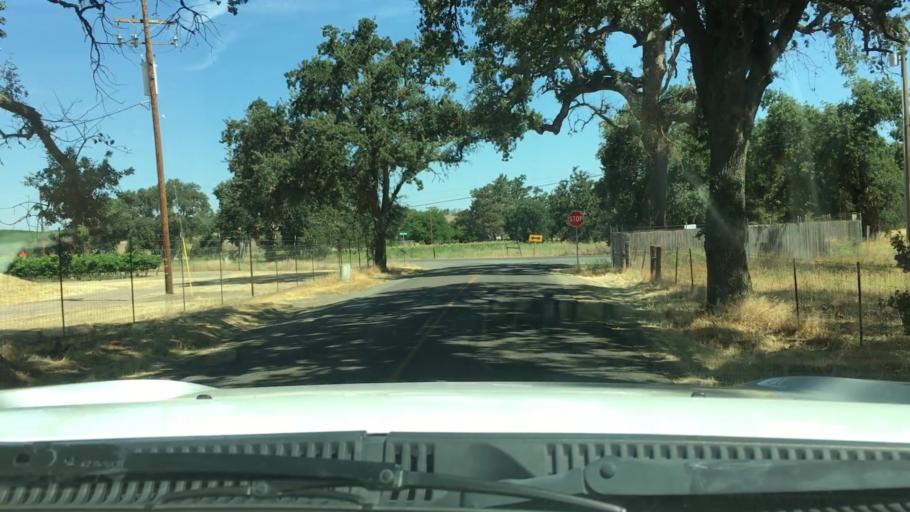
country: US
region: California
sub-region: San Luis Obispo County
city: Paso Robles
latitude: 35.5732
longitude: -120.6083
